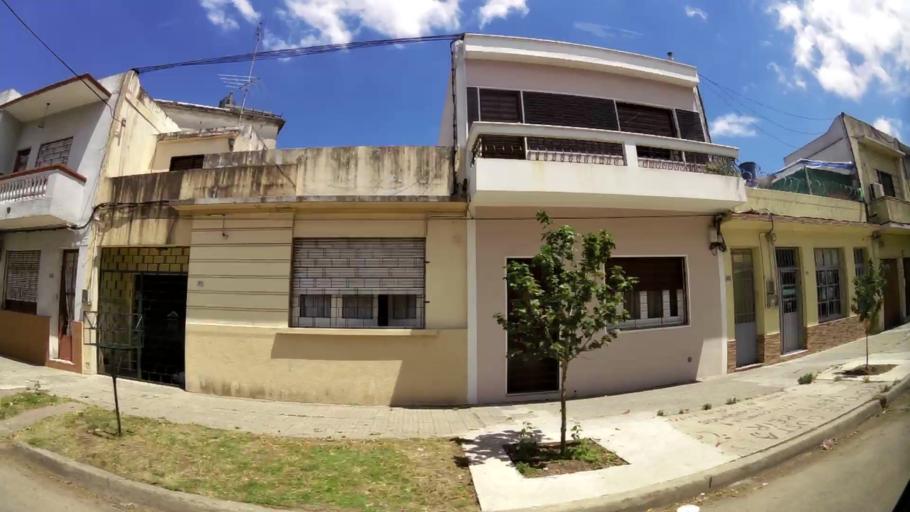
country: UY
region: Montevideo
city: Montevideo
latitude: -34.8688
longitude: -56.1909
